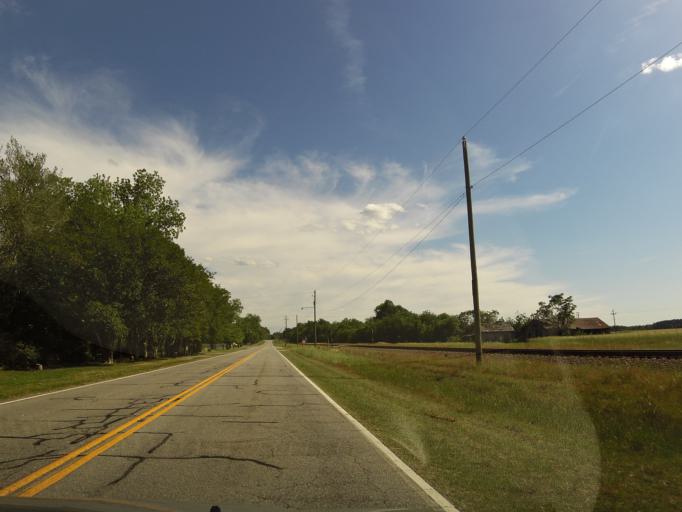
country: US
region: South Carolina
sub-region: Bamberg County
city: Denmark
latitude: 33.2251
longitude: -81.1751
